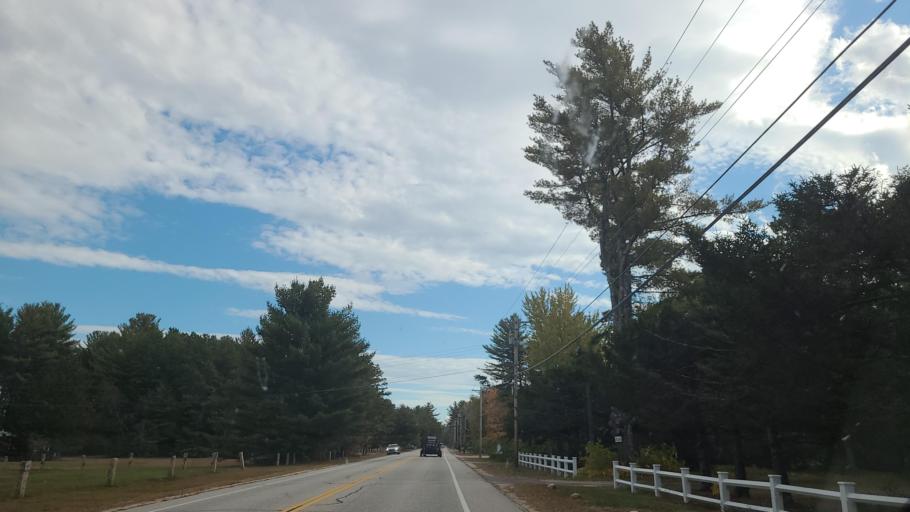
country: US
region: New Hampshire
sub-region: Carroll County
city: North Conway
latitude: 44.0439
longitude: -71.1473
